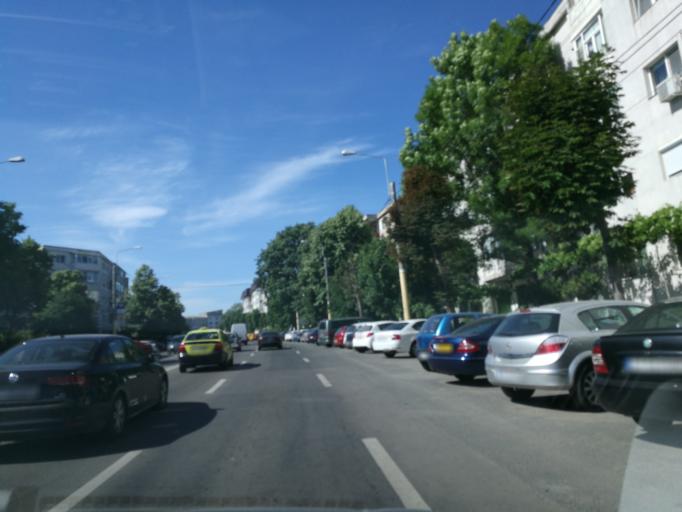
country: RO
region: Constanta
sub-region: Municipiul Constanta
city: Constanta
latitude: 44.1986
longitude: 28.6246
